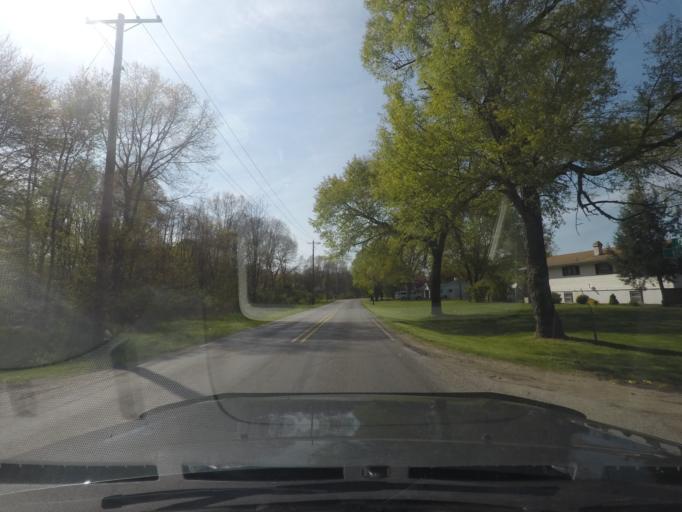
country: US
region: Indiana
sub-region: Elkhart County
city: Elkhart
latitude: 41.7074
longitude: -86.0193
